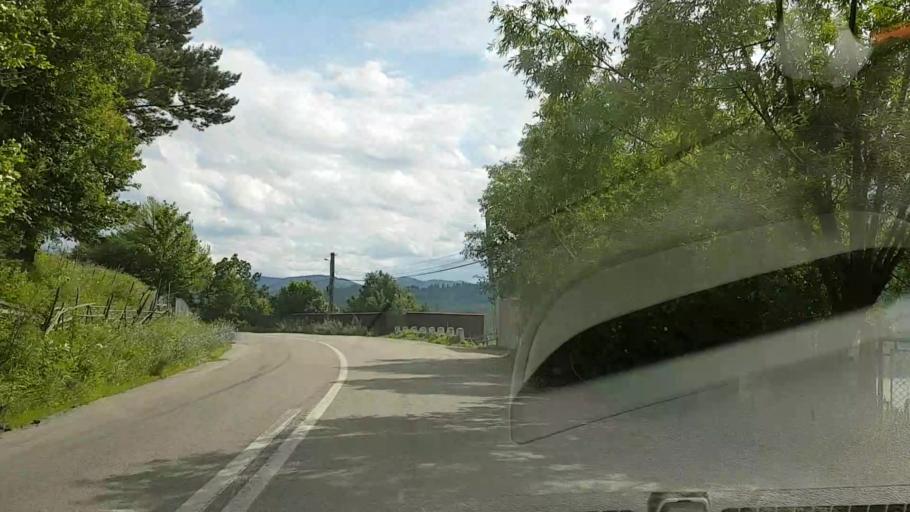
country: RO
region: Neamt
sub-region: Comuna Hangu
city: Hangu
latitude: 47.0306
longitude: 26.0658
